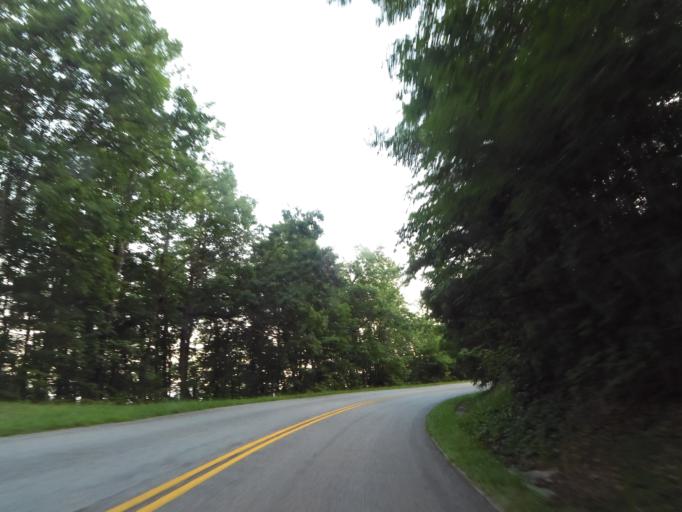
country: US
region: Tennessee
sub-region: Blount County
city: Maryville
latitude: 35.6273
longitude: -83.9499
